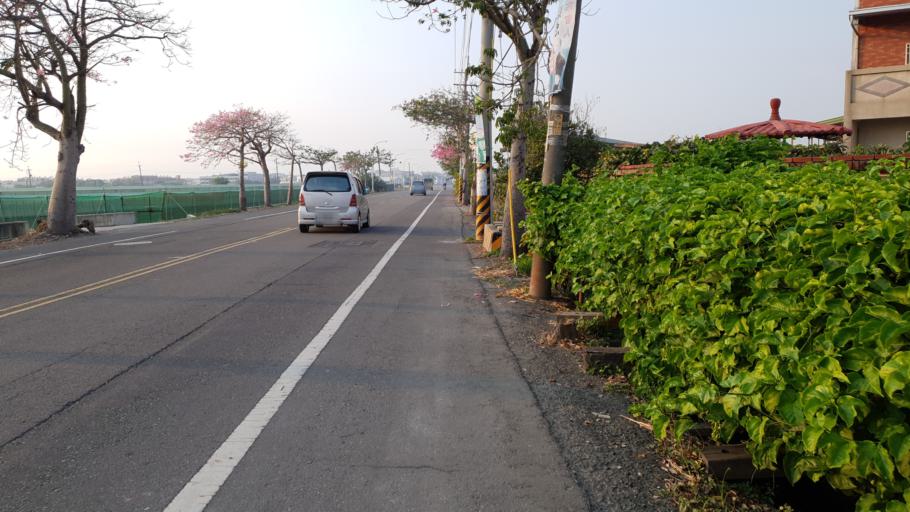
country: TW
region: Taiwan
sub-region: Yunlin
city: Douliu
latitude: 23.7636
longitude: 120.4177
